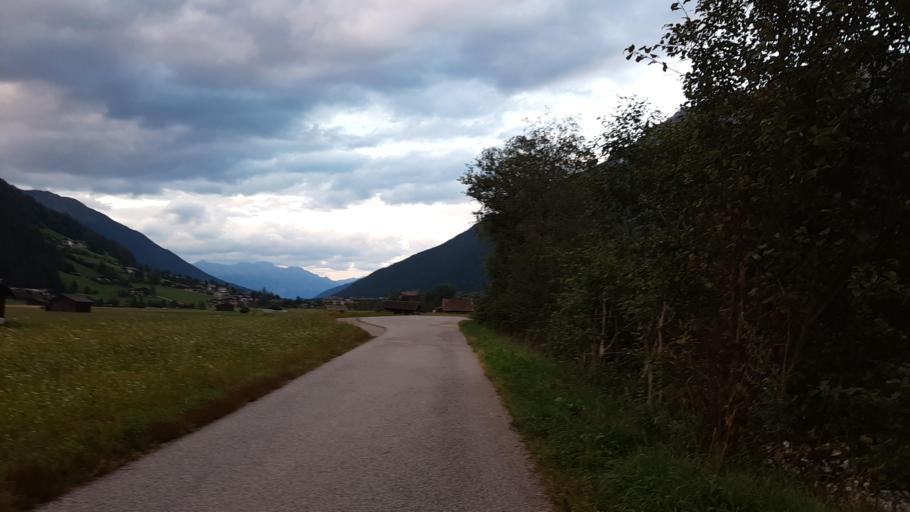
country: AT
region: Tyrol
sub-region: Politischer Bezirk Innsbruck Land
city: Neustift im Stubaital
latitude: 47.1129
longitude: 11.3171
